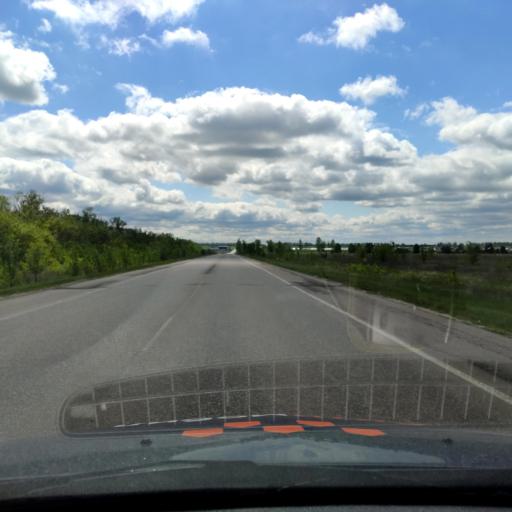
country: RU
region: Voronezj
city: Novaya Usman'
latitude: 51.6130
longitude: 39.3369
